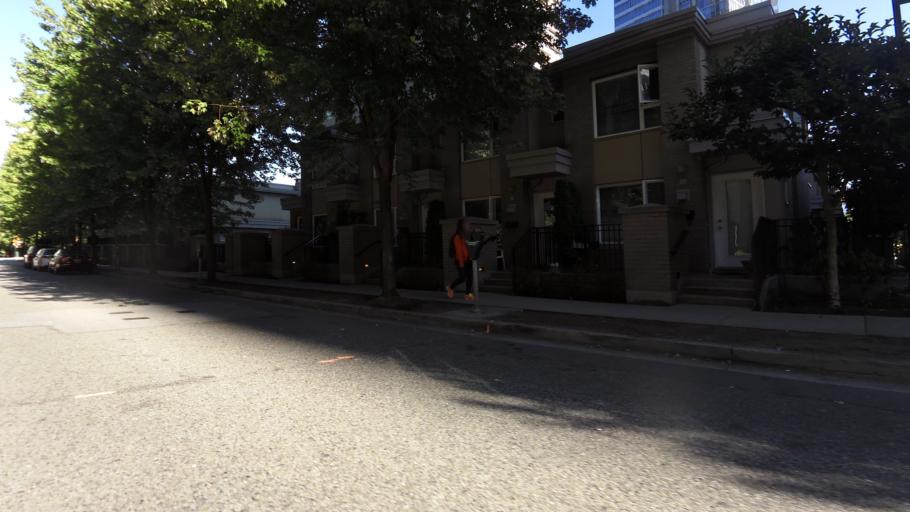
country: CA
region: British Columbia
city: West End
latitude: 49.2891
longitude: -123.1234
